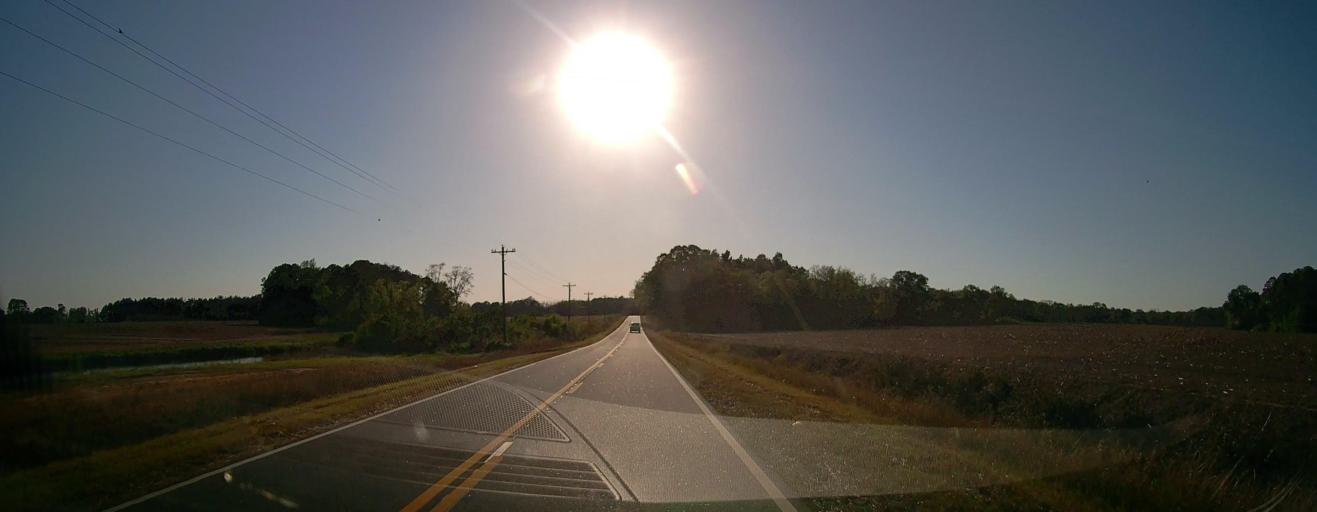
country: US
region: Georgia
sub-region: Ben Hill County
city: Fitzgerald
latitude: 31.6563
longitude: -83.1658
